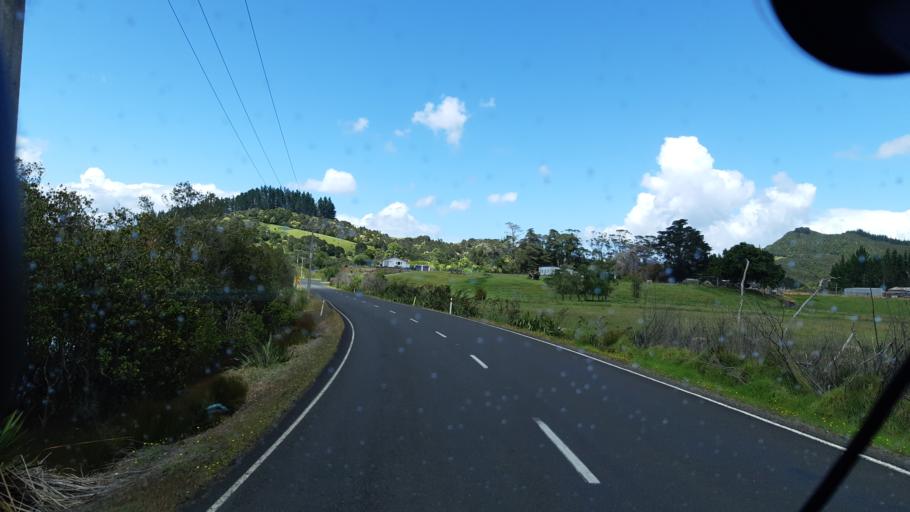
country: NZ
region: Northland
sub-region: Far North District
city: Taipa
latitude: -35.2719
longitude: 173.5222
